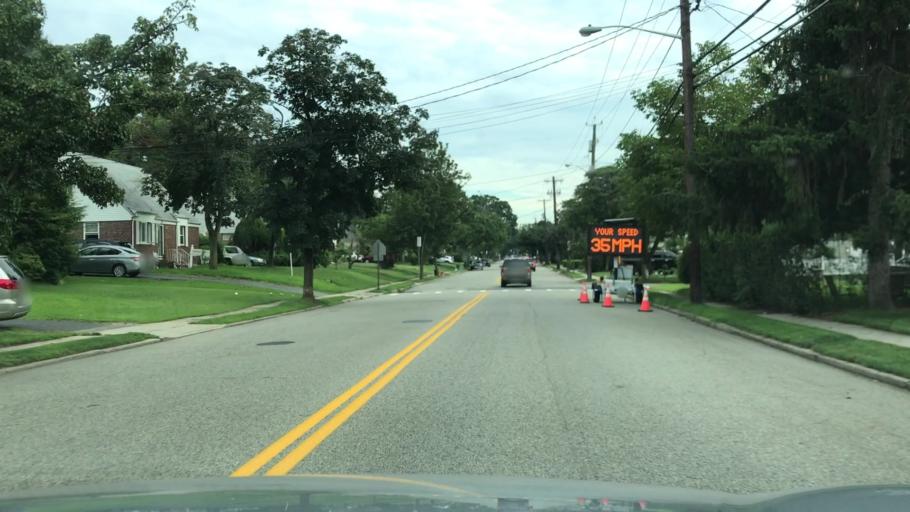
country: US
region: New Jersey
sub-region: Bergen County
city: New Milford
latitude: 40.9362
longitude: -74.0167
